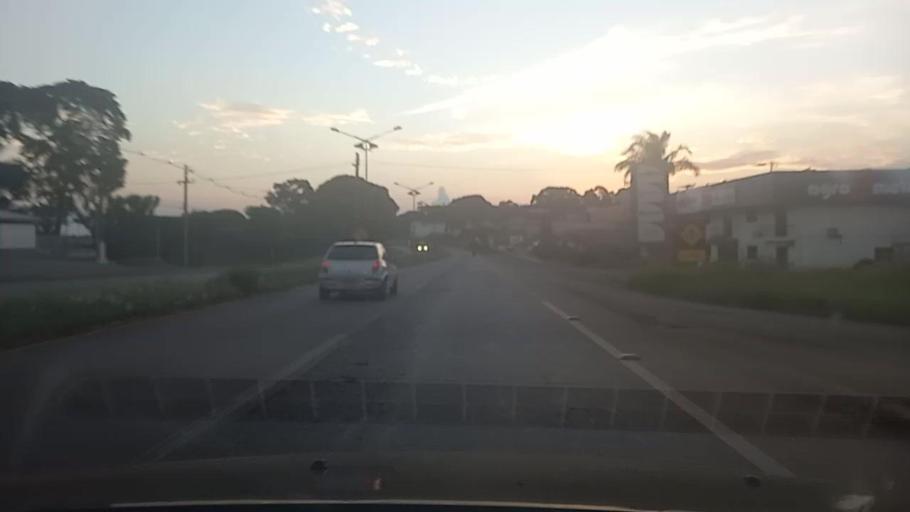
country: BR
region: Rio Grande do Sul
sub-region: Passo Fundo
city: Passo Fundo
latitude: -28.2732
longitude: -52.4444
